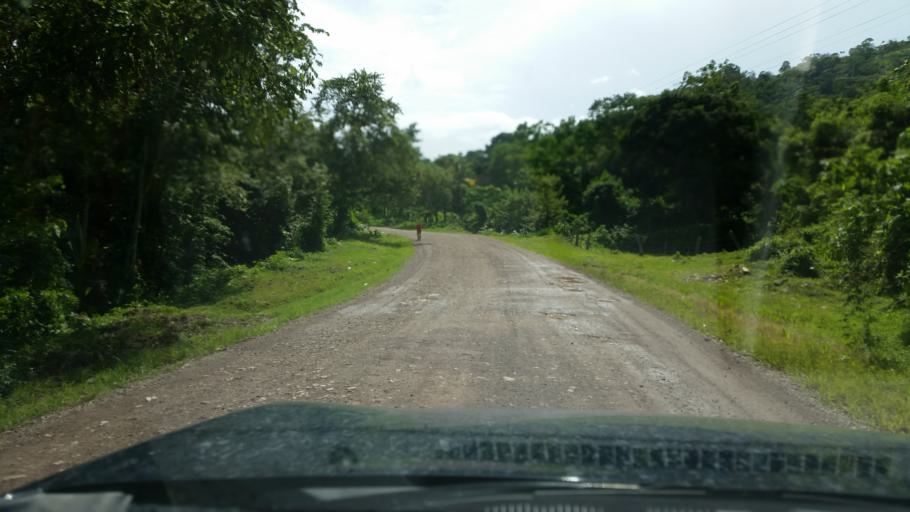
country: NI
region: Atlantico Norte (RAAN)
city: Siuna
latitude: 13.6819
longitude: -84.6417
